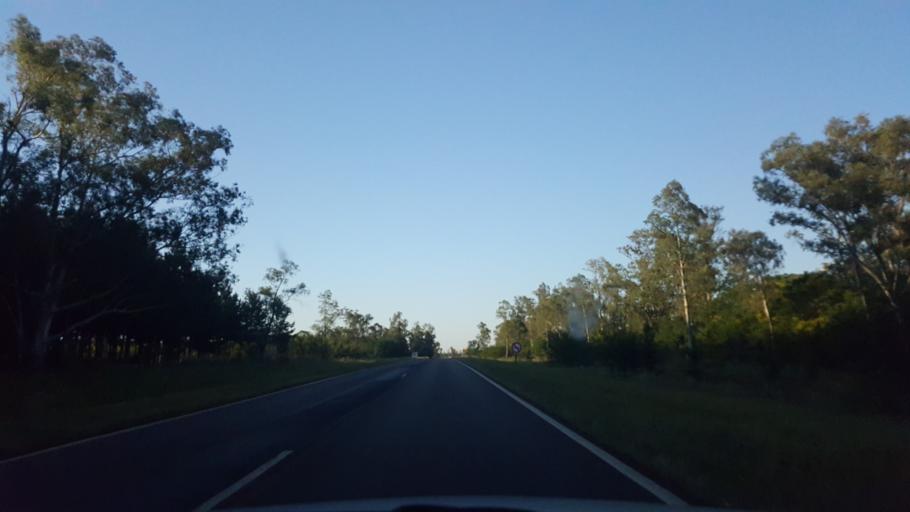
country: AR
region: Corrientes
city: Santo Tome
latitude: -28.4936
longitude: -56.1138
